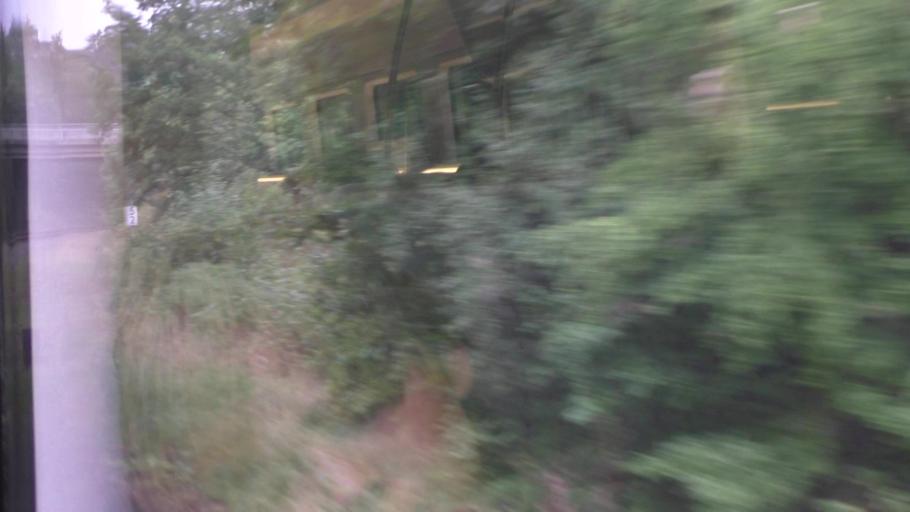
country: DE
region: Saxony
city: Eibau
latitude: 50.9750
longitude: 14.6554
